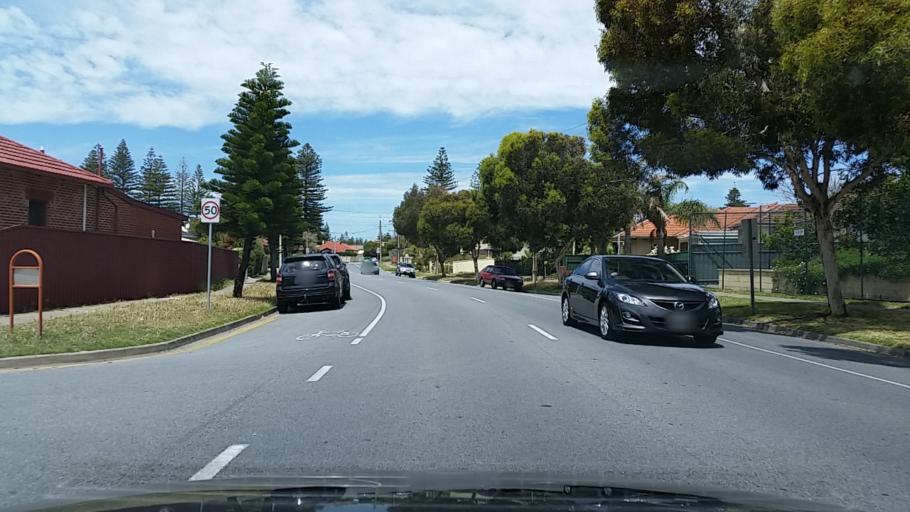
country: AU
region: South Australia
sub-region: Charles Sturt
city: Henley Beach
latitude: -34.9148
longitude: 138.4941
